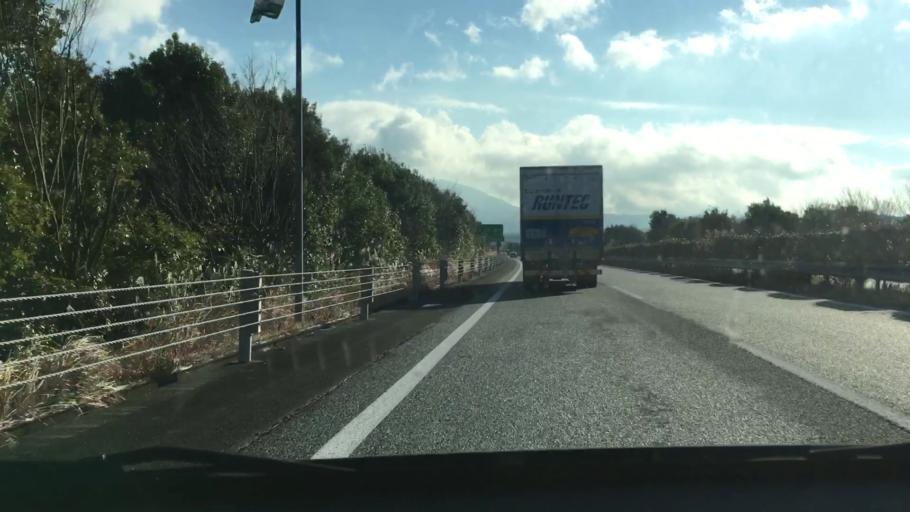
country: JP
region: Kumamoto
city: Hitoyoshi
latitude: 32.0585
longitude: 130.8030
